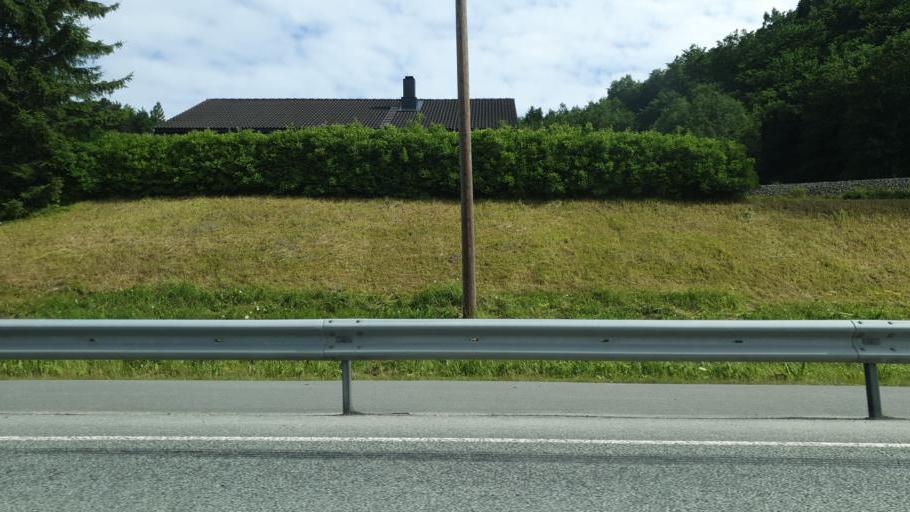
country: NO
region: Sor-Trondelag
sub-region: Melhus
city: Lundamo
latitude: 63.2196
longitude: 10.3030
